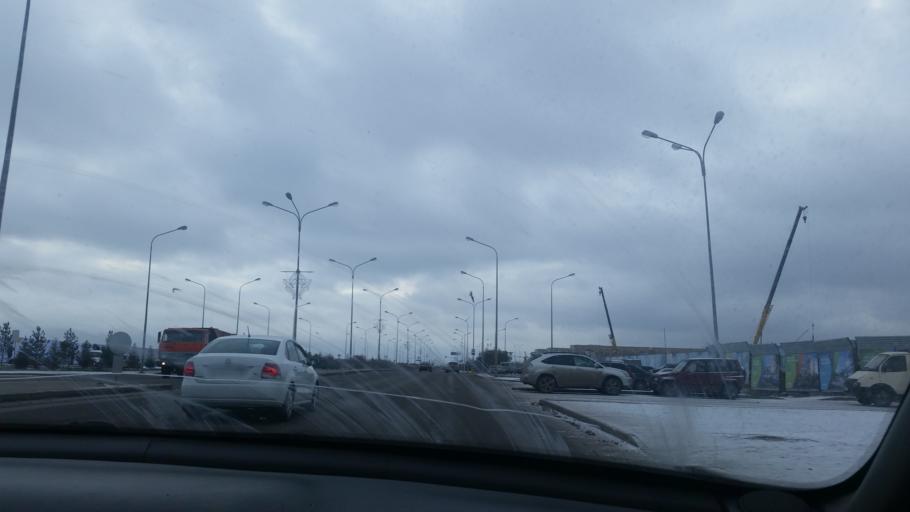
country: KZ
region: Astana Qalasy
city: Astana
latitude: 51.0872
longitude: 71.4238
